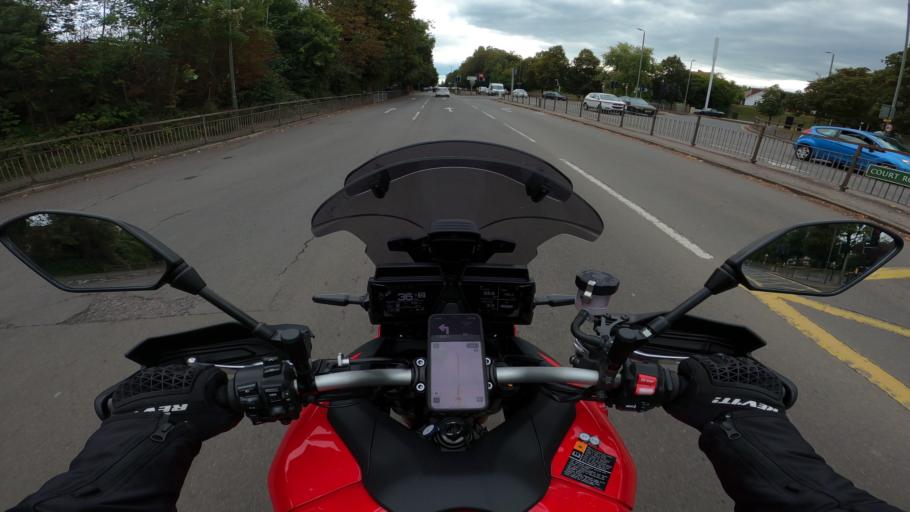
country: GB
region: England
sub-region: Greater London
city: Orpington
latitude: 51.3702
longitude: 0.1039
